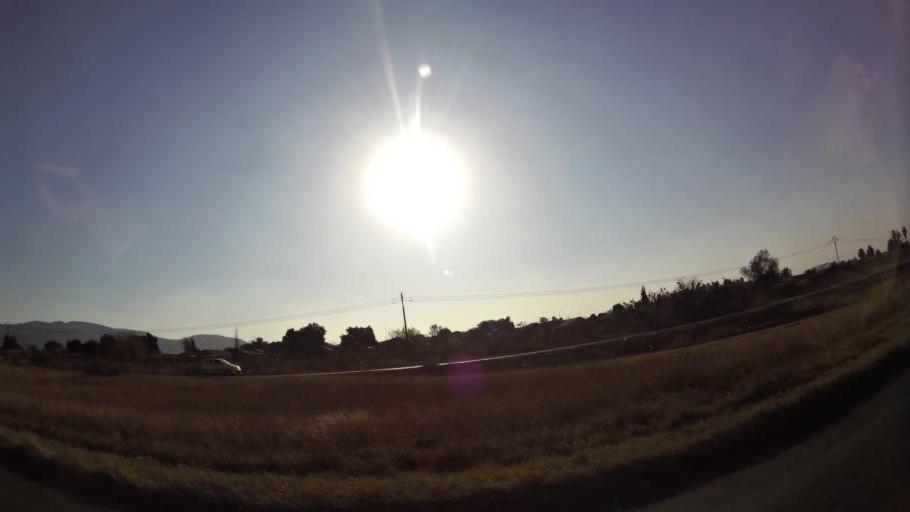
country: ZA
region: North-West
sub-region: Bojanala Platinum District Municipality
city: Rustenburg
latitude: -25.6474
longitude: 27.2264
